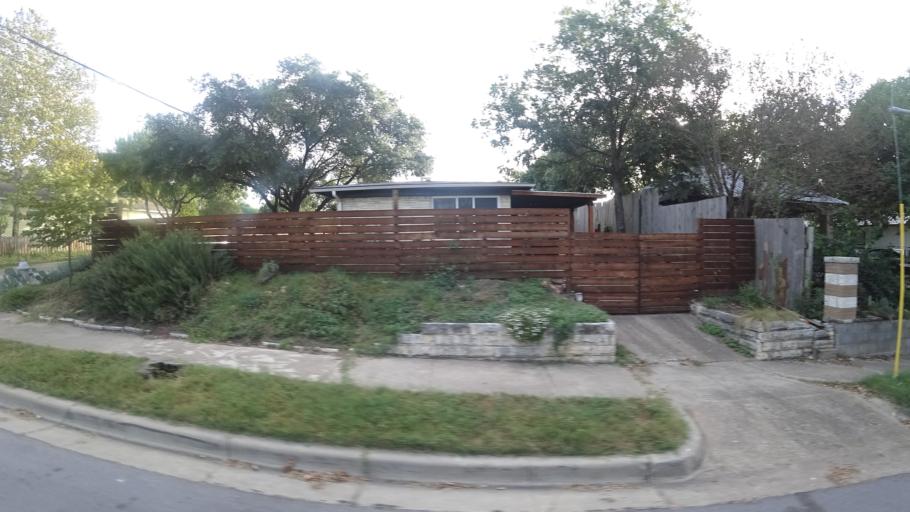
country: US
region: Texas
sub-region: Travis County
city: Austin
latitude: 30.2785
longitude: -97.7138
